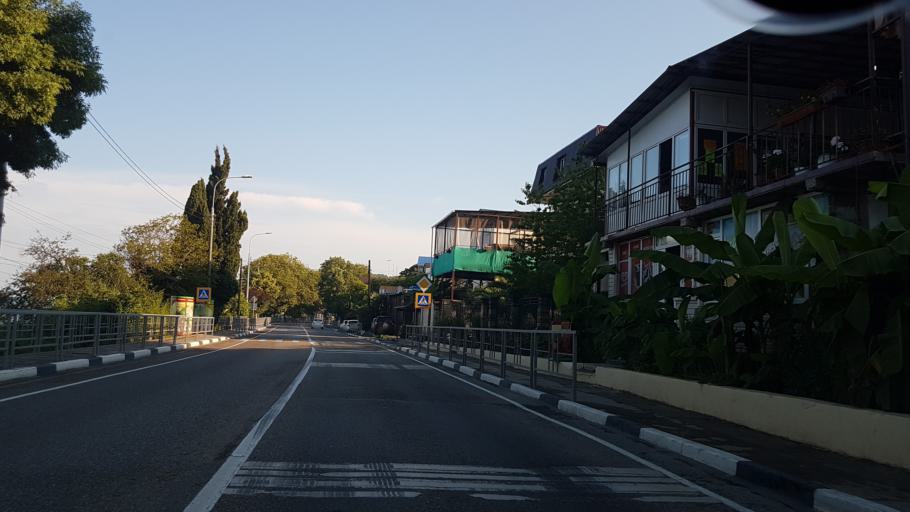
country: RU
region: Krasnodarskiy
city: Gornoye Loo
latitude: 43.6893
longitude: 39.5940
